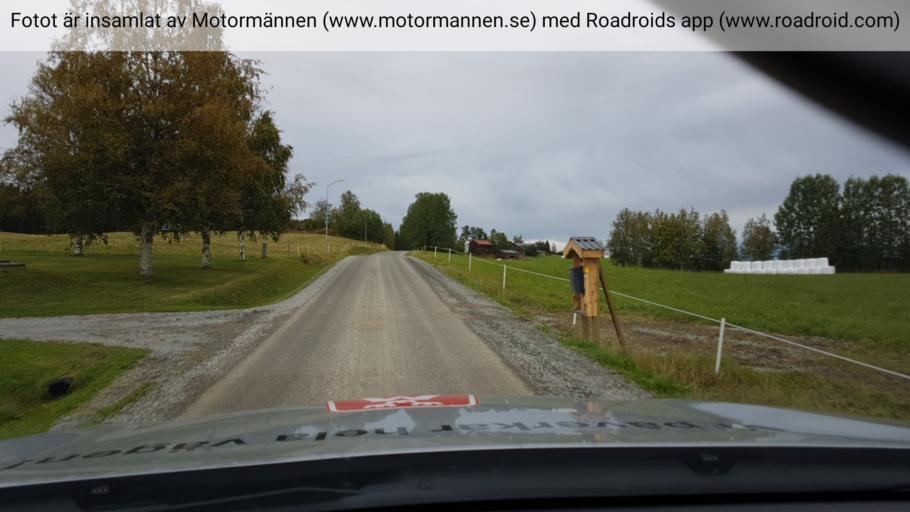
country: SE
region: Jaemtland
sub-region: Bergs Kommun
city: Hoverberg
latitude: 62.9586
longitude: 14.2653
